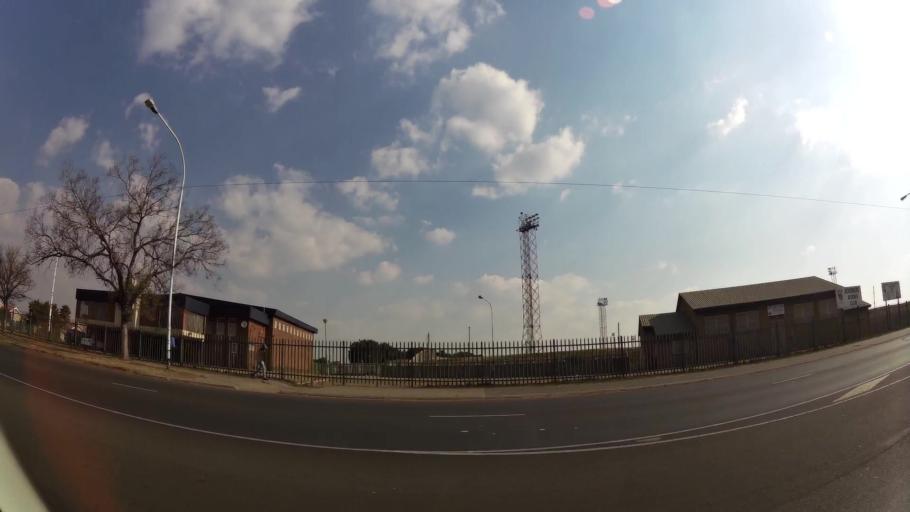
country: ZA
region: Gauteng
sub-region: Ekurhuleni Metropolitan Municipality
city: Boksburg
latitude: -26.2268
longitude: 28.2534
